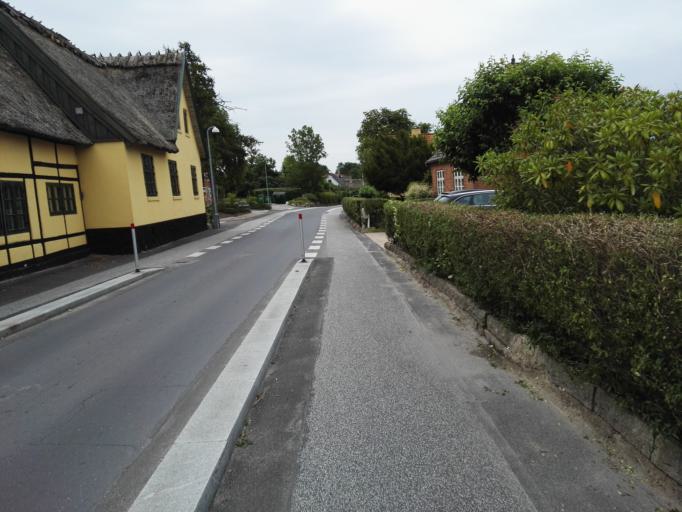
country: DK
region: Zealand
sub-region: Roskilde Kommune
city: Jyllinge
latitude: 55.7520
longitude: 12.1031
